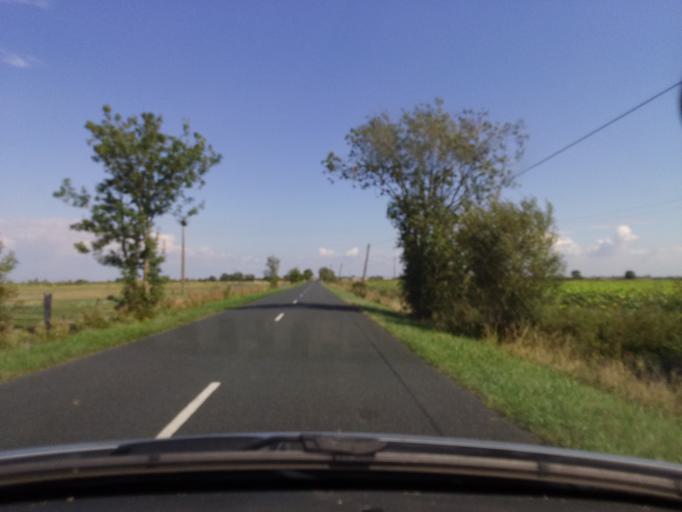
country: FR
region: Pays de la Loire
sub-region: Departement de la Vendee
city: Triaize
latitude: 46.3971
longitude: -1.2209
